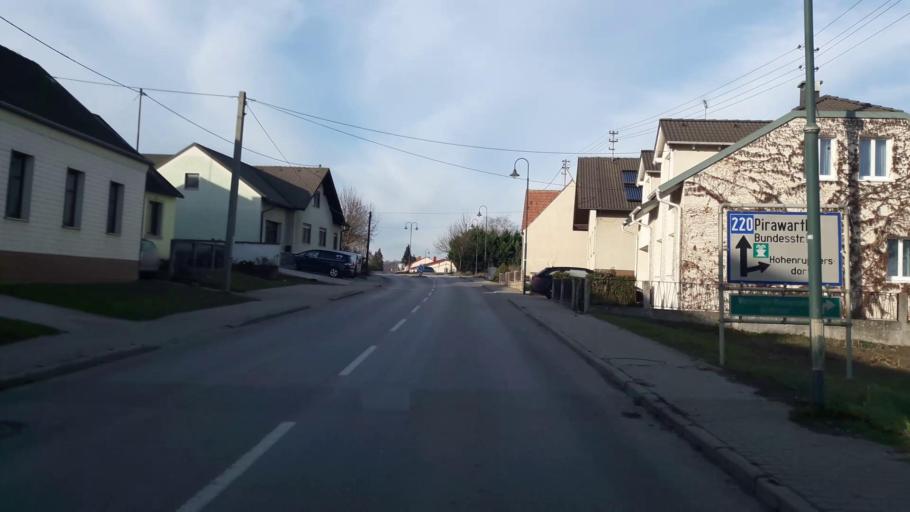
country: AT
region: Lower Austria
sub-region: Politischer Bezirk Ganserndorf
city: Gross-Schweinbarth
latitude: 48.4194
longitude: 16.6309
